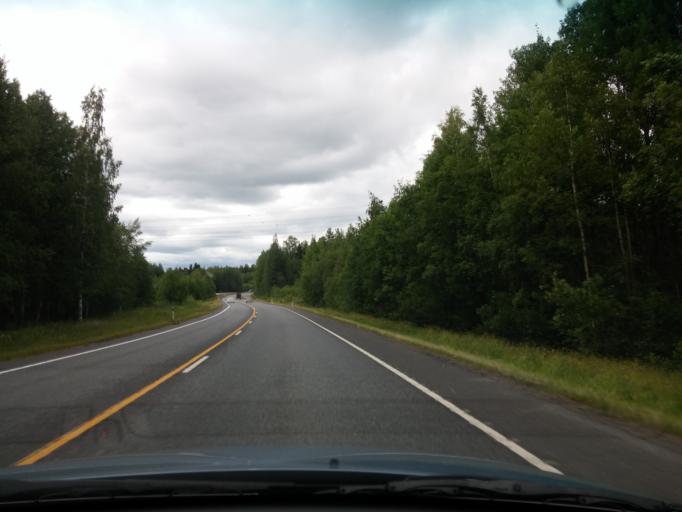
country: FI
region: Uusimaa
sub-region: Porvoo
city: Porvoo
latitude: 60.4275
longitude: 25.5787
